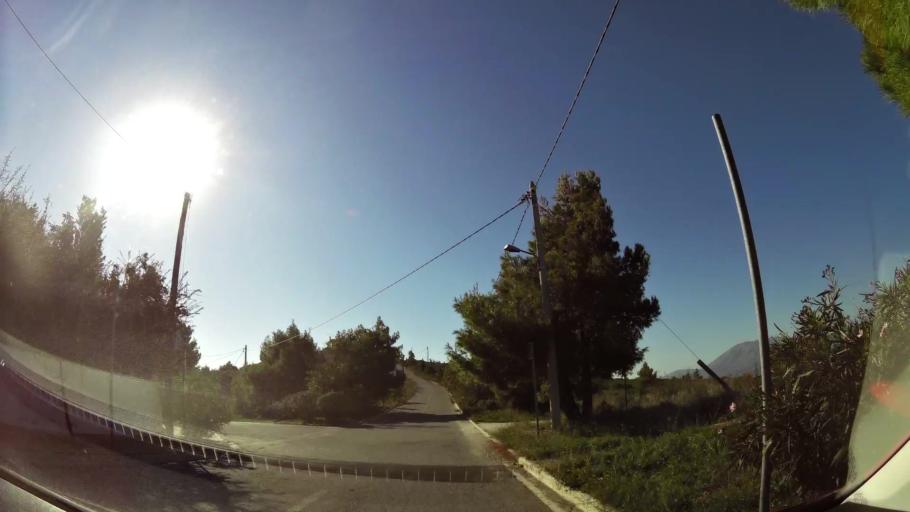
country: GR
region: Attica
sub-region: Nomarchia Anatolikis Attikis
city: Anthousa
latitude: 38.0329
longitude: 23.8920
